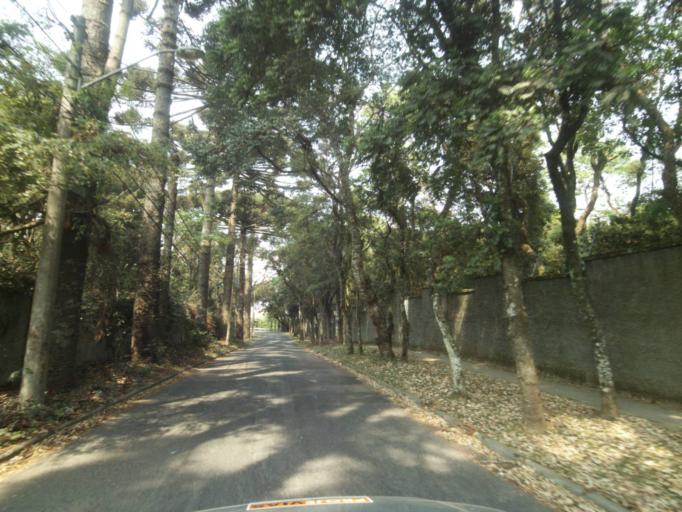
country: BR
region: Parana
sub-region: Pinhais
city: Pinhais
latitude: -25.4783
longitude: -49.2184
